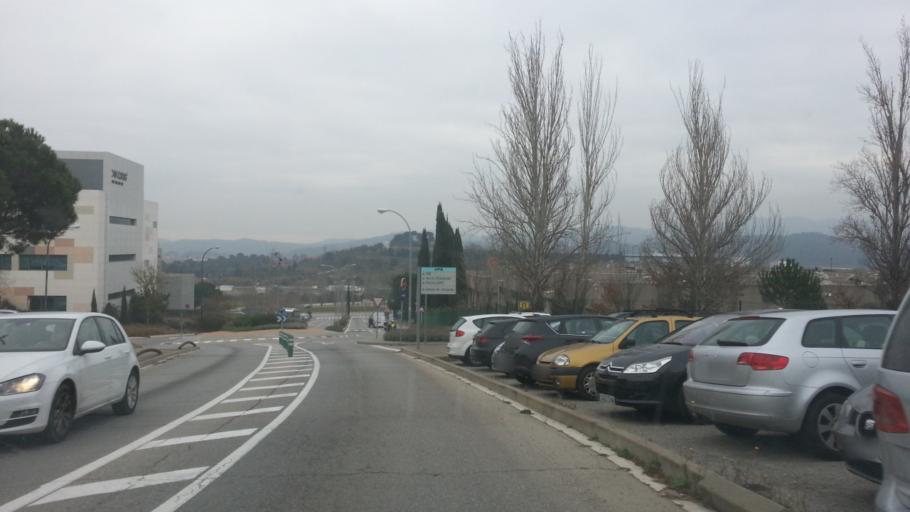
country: ES
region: Catalonia
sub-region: Provincia de Barcelona
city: Barbera del Valles
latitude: 41.4975
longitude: 2.1070
